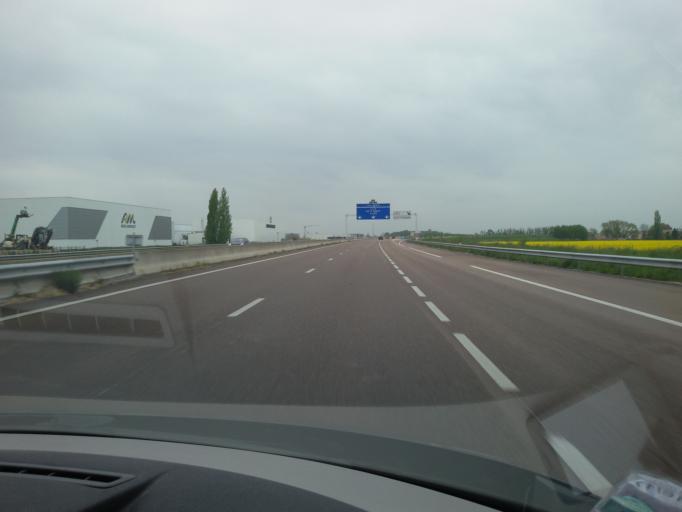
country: FR
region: Bourgogne
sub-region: Departement de la Cote-d'Or
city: Nuits-Saint-Georges
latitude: 47.1236
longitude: 4.9672
